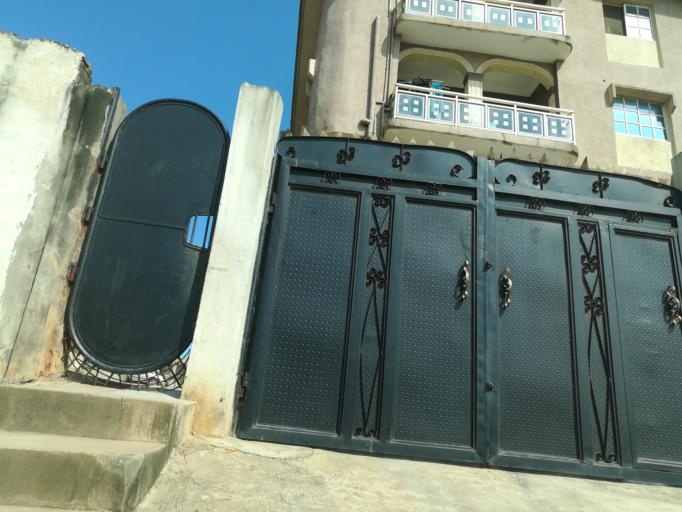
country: NG
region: Lagos
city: Ikorodu
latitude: 6.6044
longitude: 3.5044
